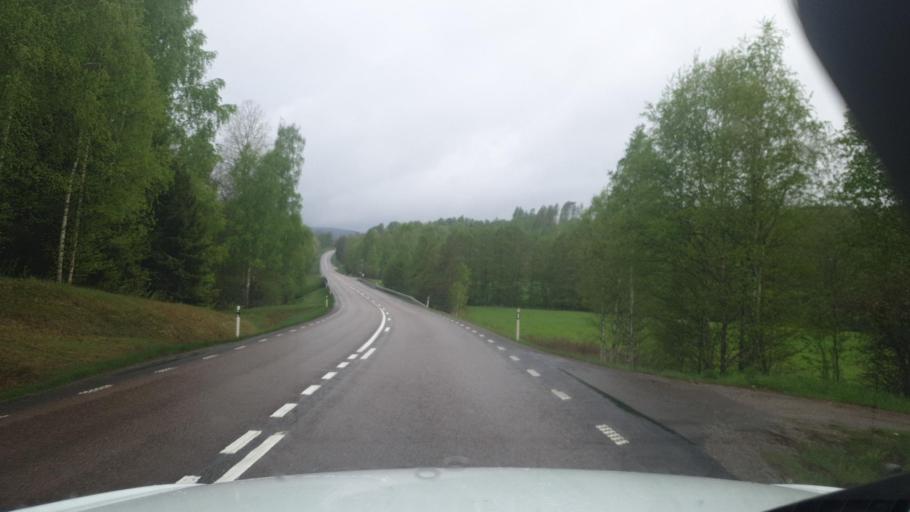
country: SE
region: Vaermland
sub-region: Sunne Kommun
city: Sunne
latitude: 59.6662
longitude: 12.9067
